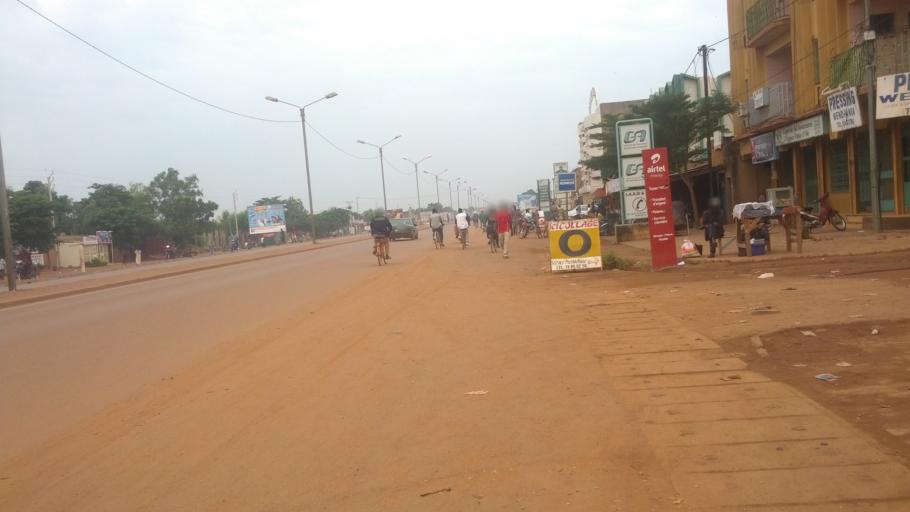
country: BF
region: Centre
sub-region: Kadiogo Province
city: Ouagadougou
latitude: 12.3330
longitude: -1.5180
